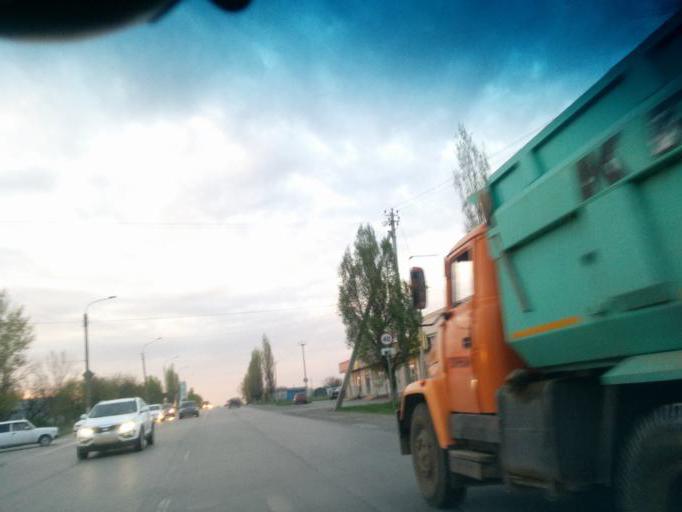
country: RU
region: Rostov
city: Krasyukovskaya
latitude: 47.4872
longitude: 40.1030
